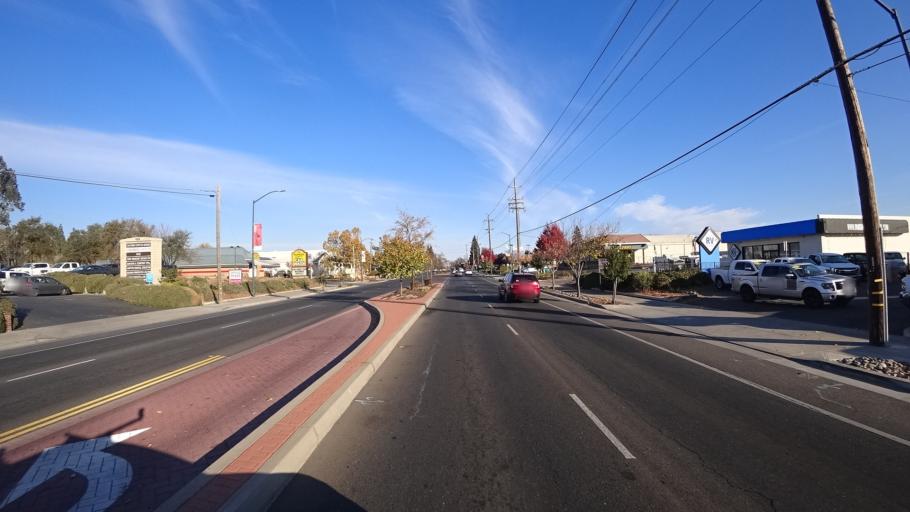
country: US
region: California
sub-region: Sacramento County
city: Citrus Heights
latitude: 38.7054
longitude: -121.2718
